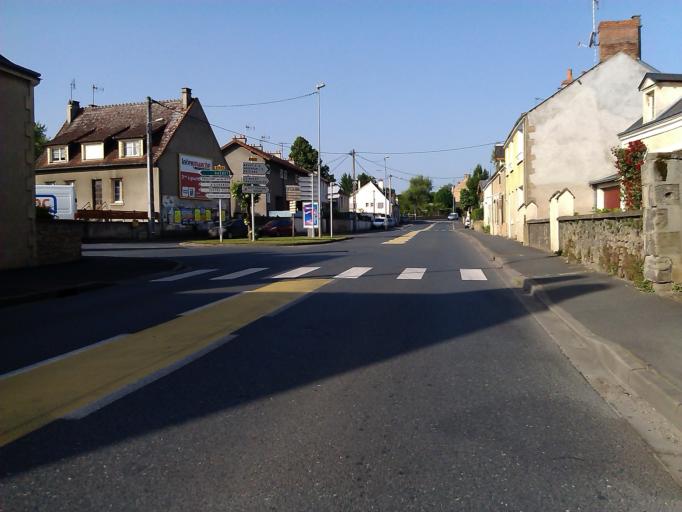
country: FR
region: Centre
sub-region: Departement de l'Indre
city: La Chatre
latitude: 46.5806
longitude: 1.9817
